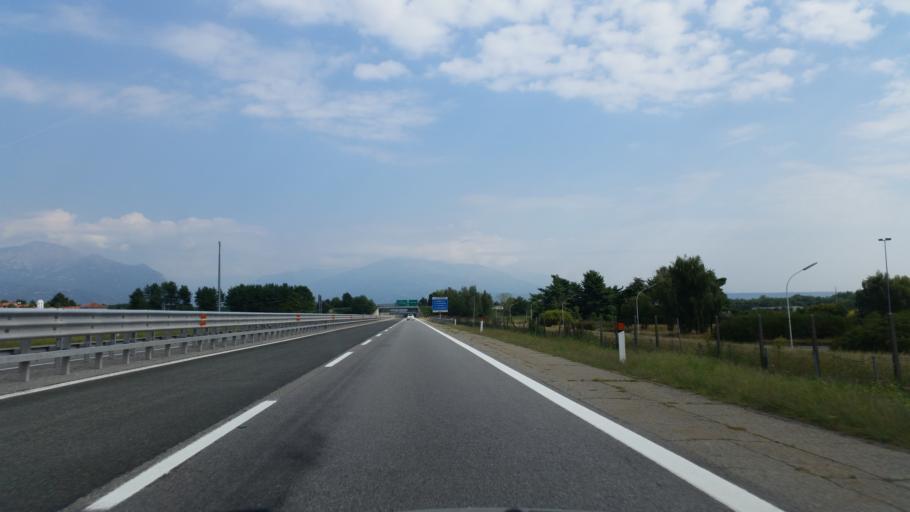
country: IT
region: Piedmont
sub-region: Provincia di Torino
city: Scarmagno
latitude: 45.3815
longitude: 7.8459
